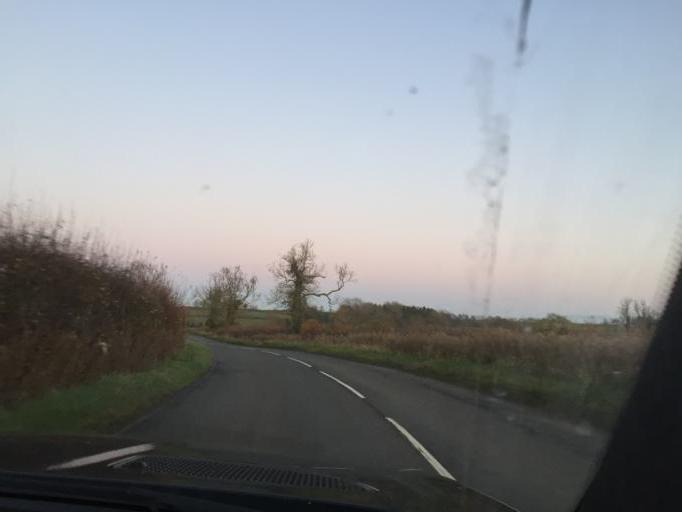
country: GB
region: England
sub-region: Northamptonshire
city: Brackley
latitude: 52.0949
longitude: -1.1194
